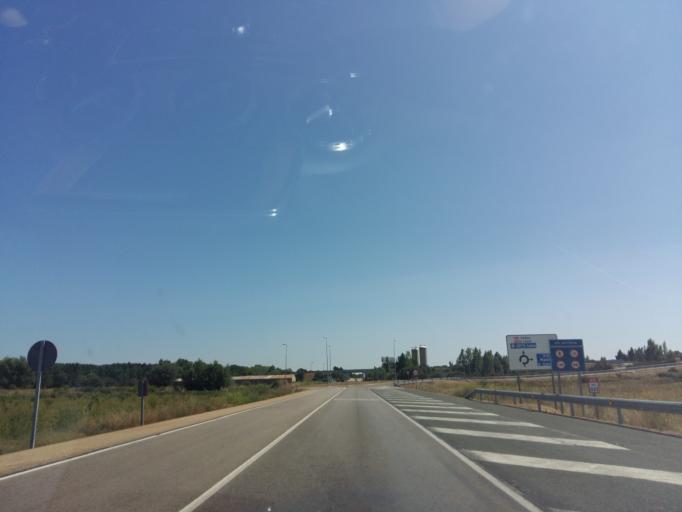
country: ES
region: Castille and Leon
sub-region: Provincia de Leon
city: Astorga
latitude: 42.4417
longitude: -6.0401
